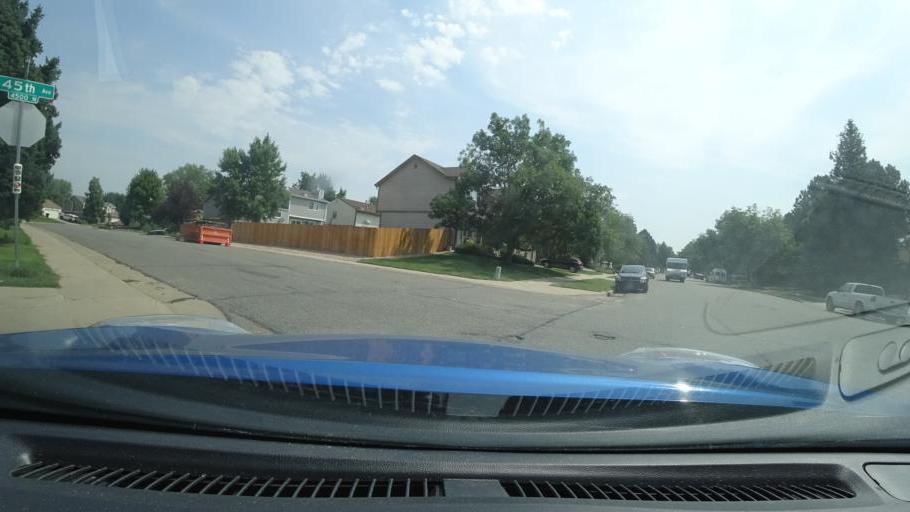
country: US
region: Colorado
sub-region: Adams County
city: Aurora
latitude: 39.7780
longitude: -104.7674
